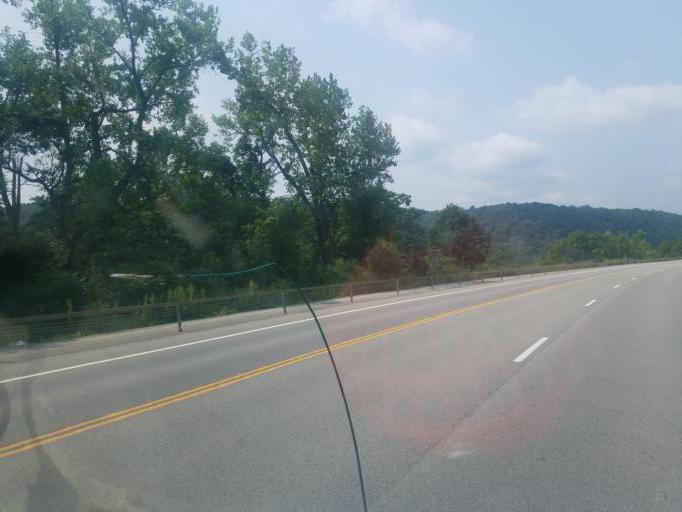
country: US
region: New York
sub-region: Herkimer County
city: Little Falls
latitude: 43.0365
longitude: -74.8316
